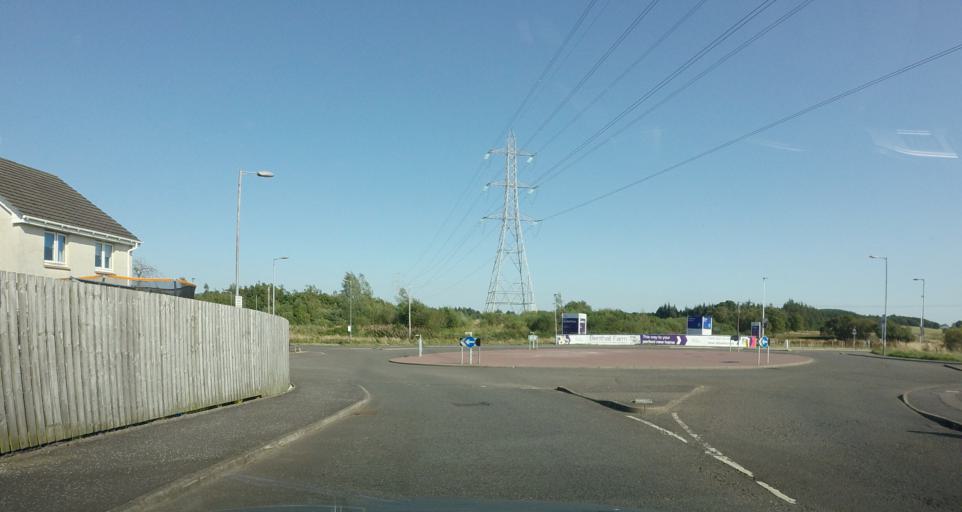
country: GB
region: Scotland
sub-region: South Lanarkshire
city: East Kilbride
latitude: 55.7407
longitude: -4.1925
